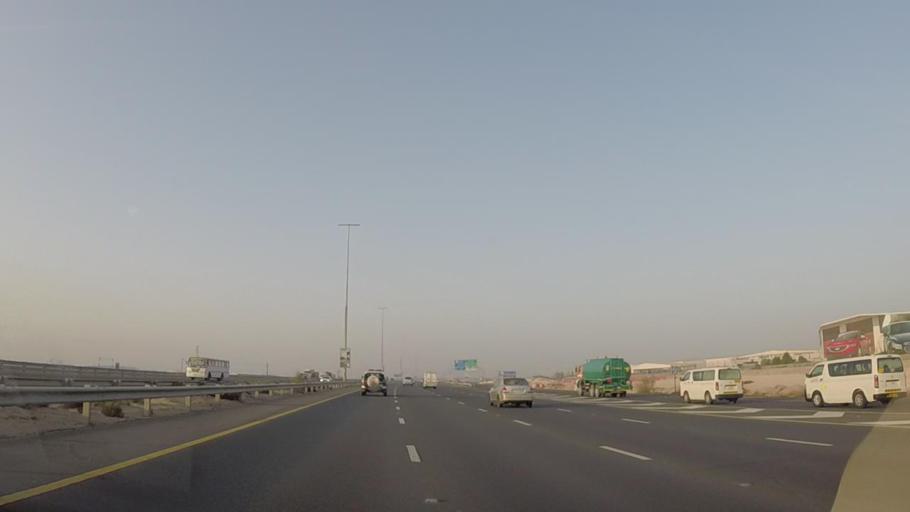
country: AE
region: Dubai
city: Dubai
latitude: 24.9515
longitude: 55.0720
